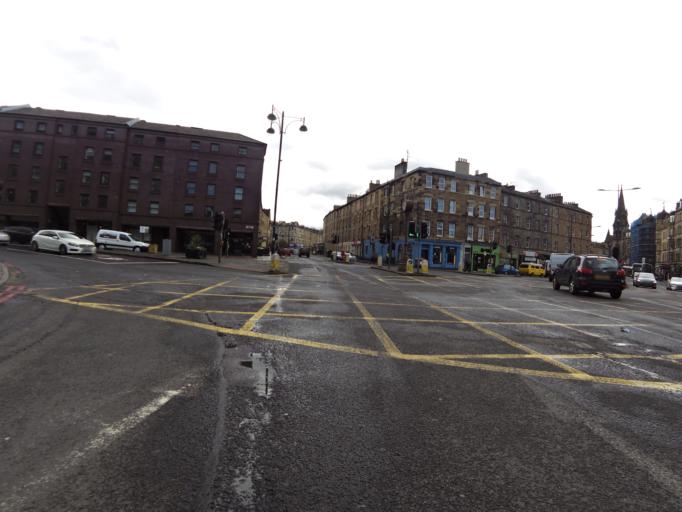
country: GB
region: Scotland
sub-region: Edinburgh
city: Edinburgh
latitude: 55.9439
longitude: -3.2038
